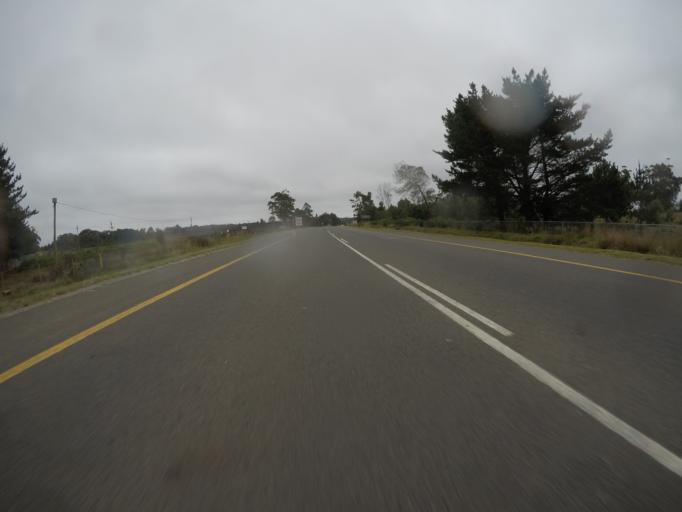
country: ZA
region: Western Cape
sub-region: Eden District Municipality
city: Plettenberg Bay
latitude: -34.0443
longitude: 23.3144
